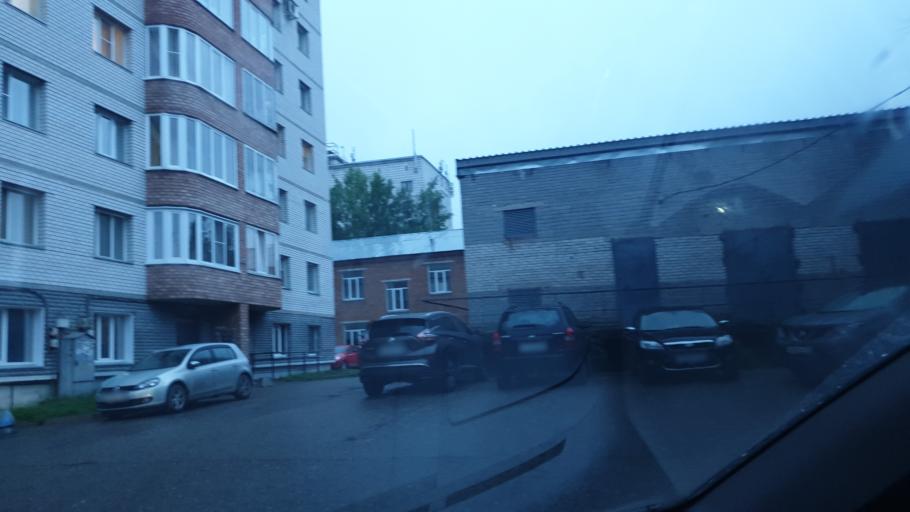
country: RU
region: Komi Republic
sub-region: Syktyvdinskiy Rayon
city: Syktyvkar
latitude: 61.6644
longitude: 50.8244
